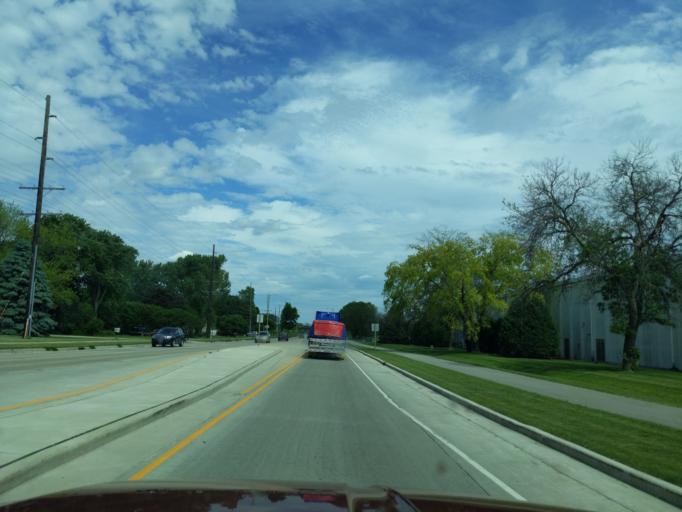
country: US
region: Wisconsin
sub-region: Dane County
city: Sun Prairie
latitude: 43.1874
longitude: -89.2409
